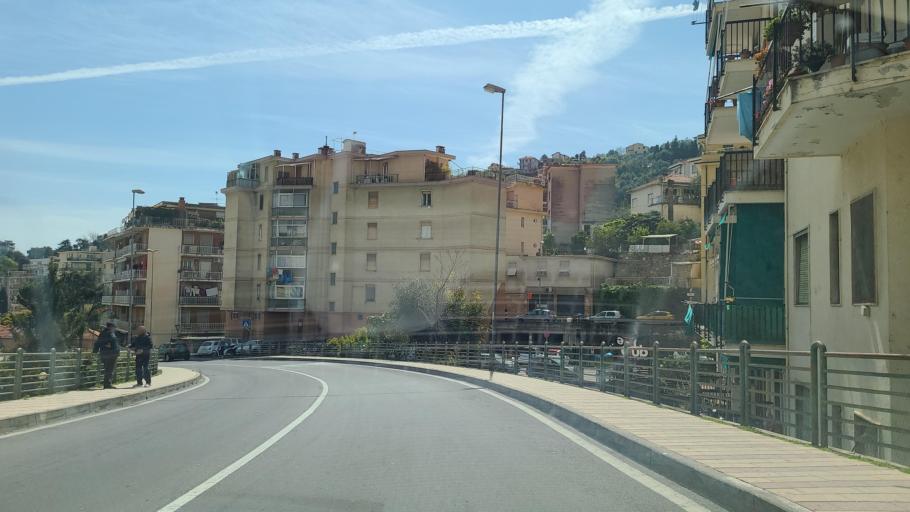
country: IT
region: Liguria
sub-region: Provincia di Imperia
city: San Remo
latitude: 43.8254
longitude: 7.7626
